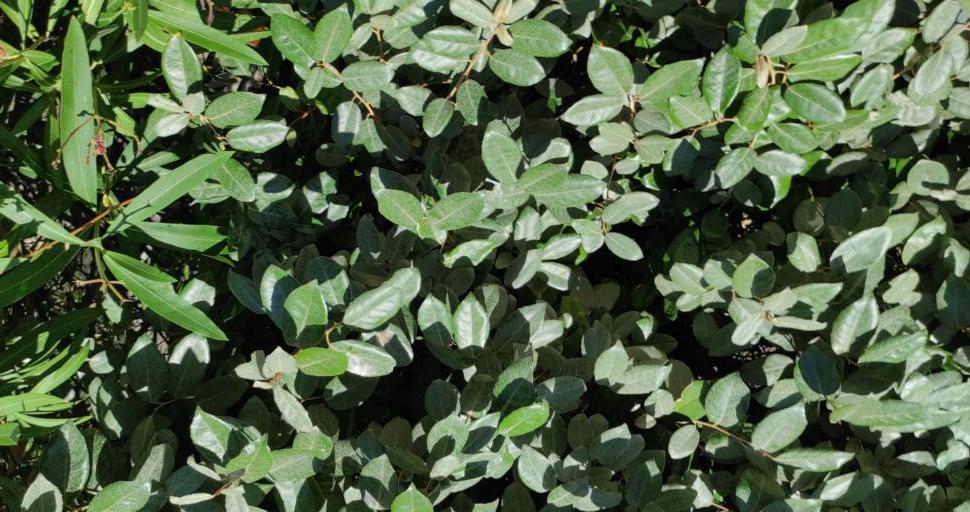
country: FR
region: Corsica
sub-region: Departement de la Corse-du-Sud
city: Alata
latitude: 41.9933
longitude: 8.6713
